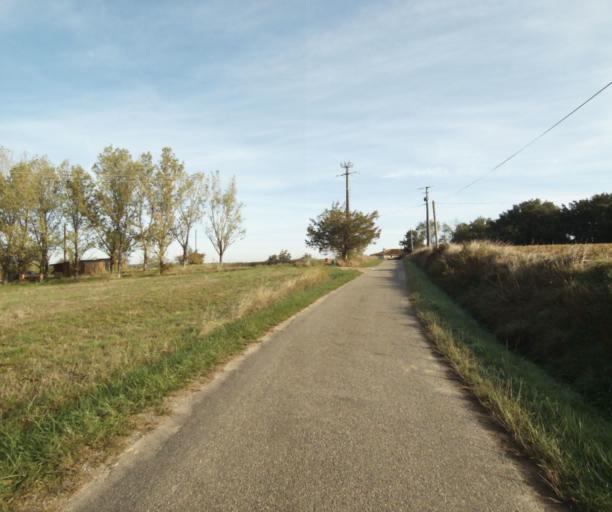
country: FR
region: Midi-Pyrenees
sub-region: Departement de la Haute-Garonne
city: Villemur-sur-Tarn
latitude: 43.9078
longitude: 1.5004
